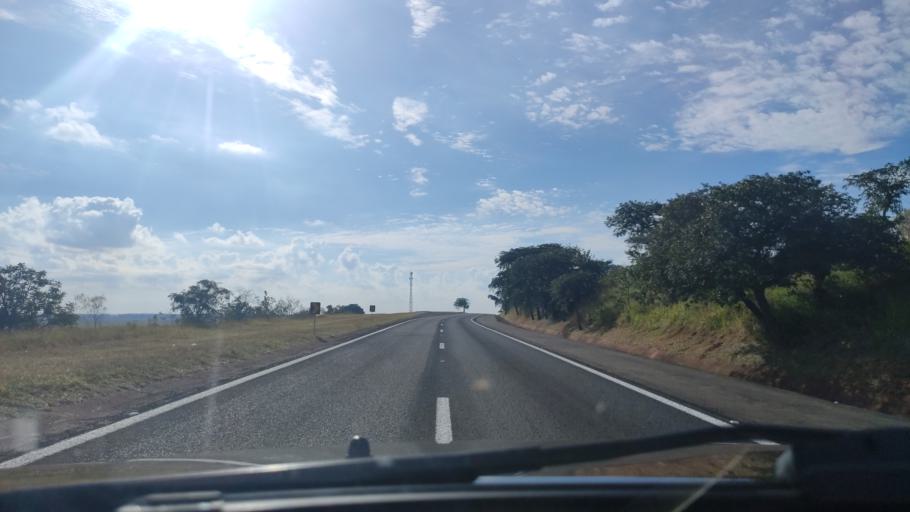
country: BR
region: Sao Paulo
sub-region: Avare
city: Avare
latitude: -22.9666
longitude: -48.8102
